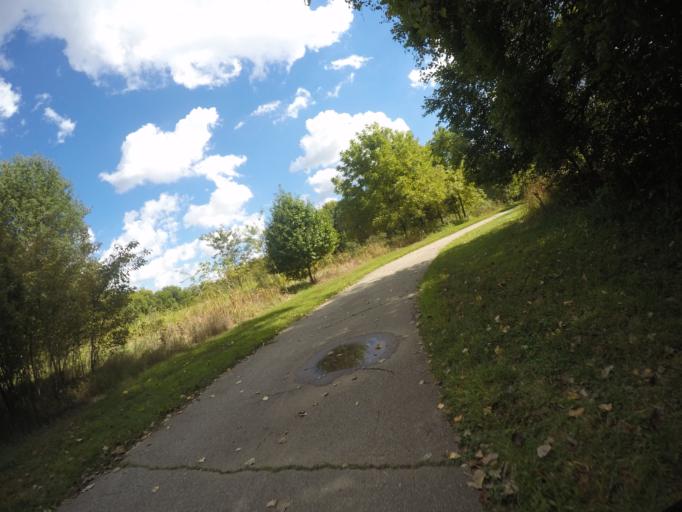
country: US
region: Kansas
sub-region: Johnson County
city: Lenexa
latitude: 38.9165
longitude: -94.7096
